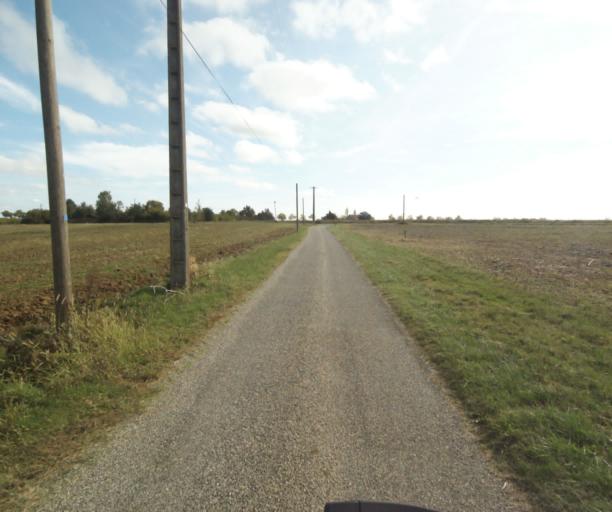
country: FR
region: Midi-Pyrenees
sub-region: Departement du Tarn-et-Garonne
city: Saint-Porquier
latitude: 43.9470
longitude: 1.1336
